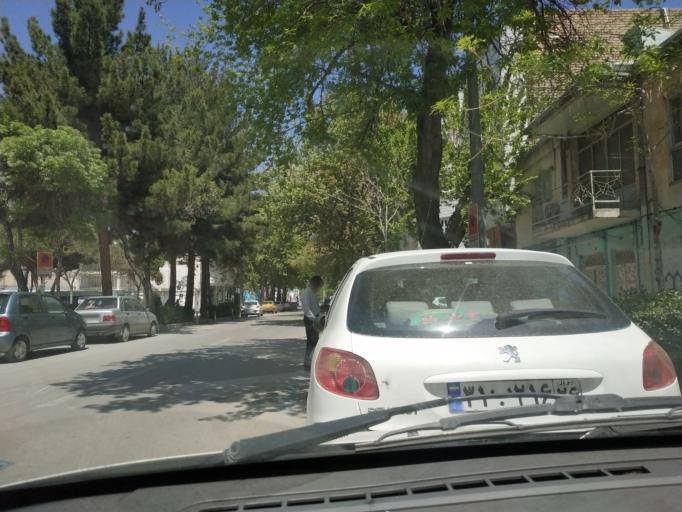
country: IR
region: Khorasan-e Shomali
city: Bojnurd
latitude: 37.4776
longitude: 57.3257
